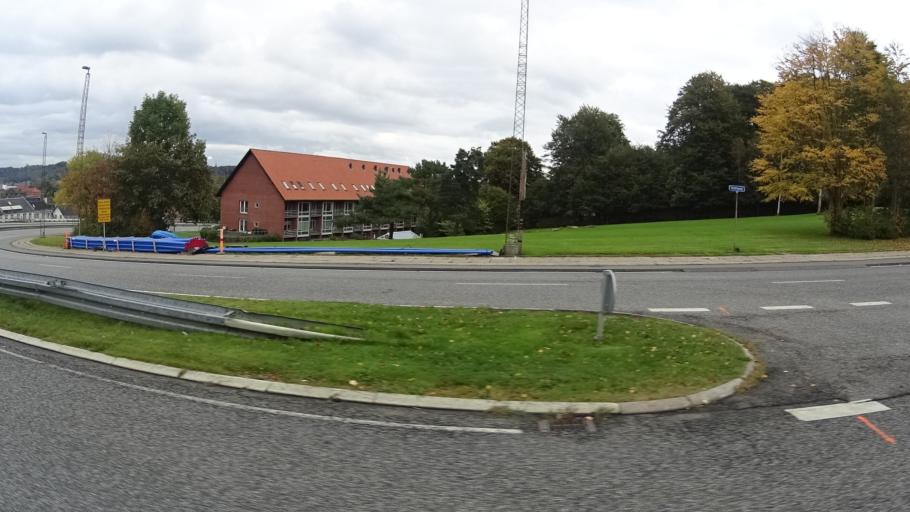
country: DK
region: South Denmark
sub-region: Vejle Kommune
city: Vejle
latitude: 55.7016
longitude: 9.5250
